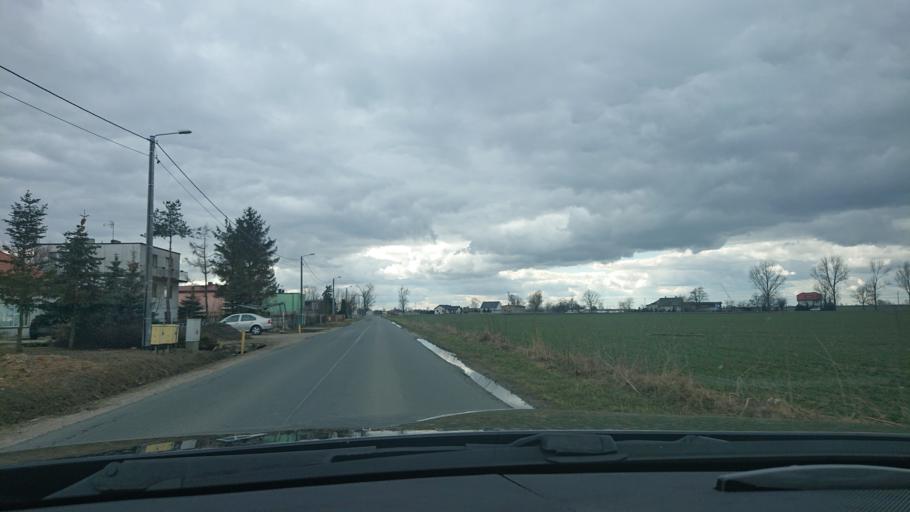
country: PL
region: Greater Poland Voivodeship
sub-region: Powiat gnieznienski
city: Gniezno
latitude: 52.5728
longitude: 17.6170
